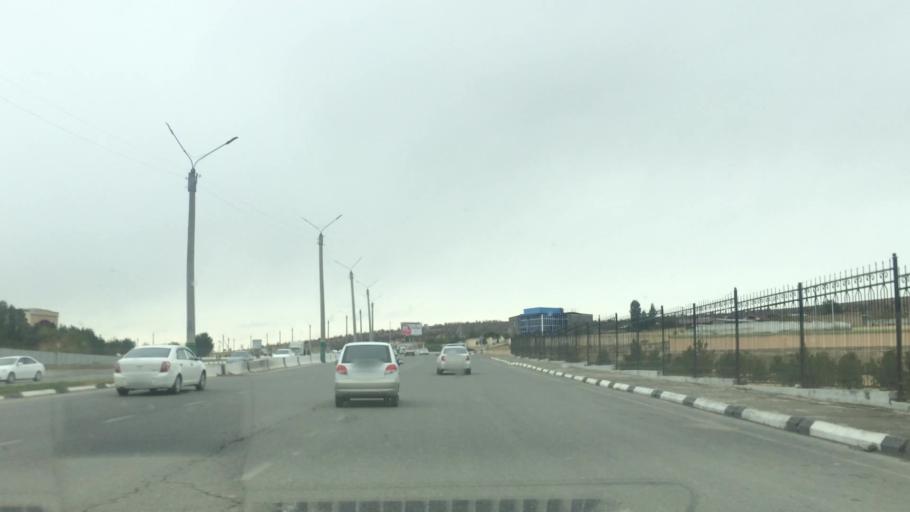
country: UZ
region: Samarqand
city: Jomboy
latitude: 39.6754
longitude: 67.0440
